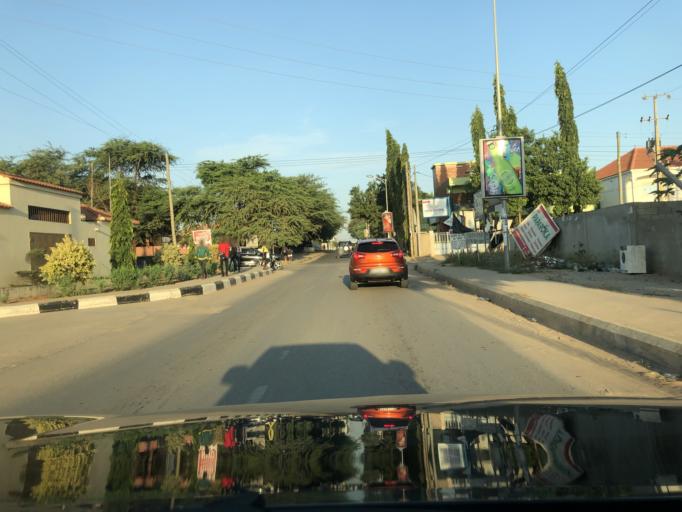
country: AO
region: Luanda
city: Luanda
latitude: -8.9466
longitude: 13.1634
